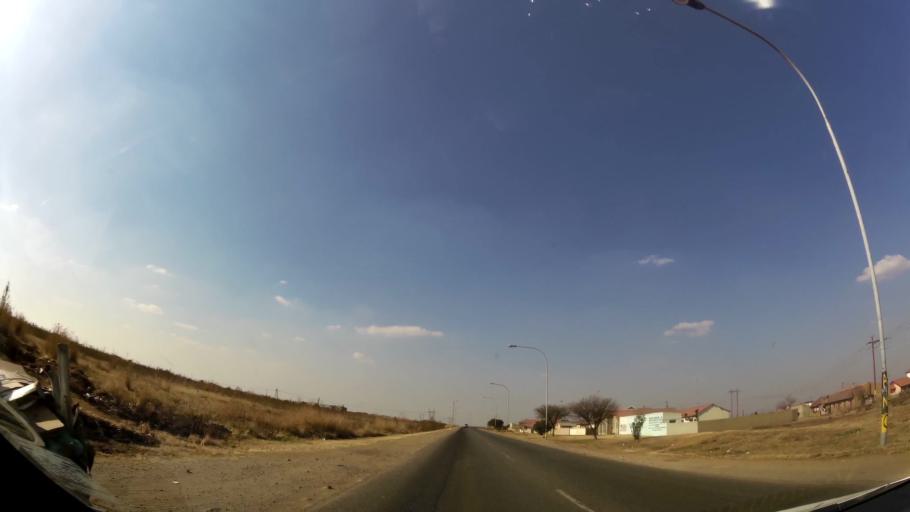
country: ZA
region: Gauteng
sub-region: Ekurhuleni Metropolitan Municipality
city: Benoni
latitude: -26.2227
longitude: 28.3213
